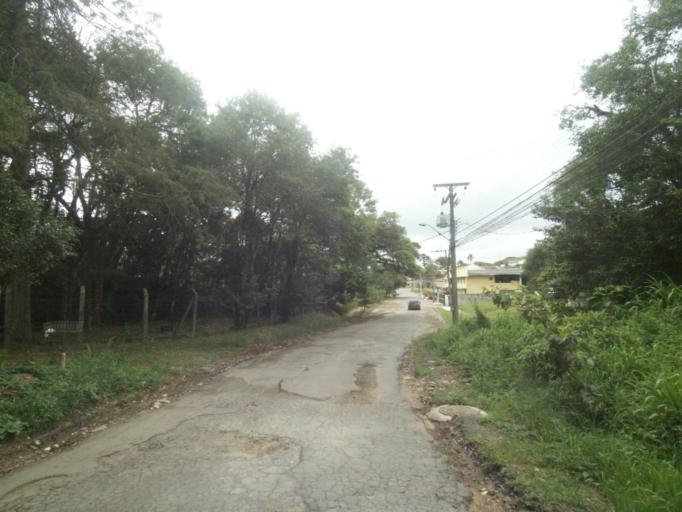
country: BR
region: Parana
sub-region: Curitiba
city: Curitiba
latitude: -25.3975
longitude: -49.2761
